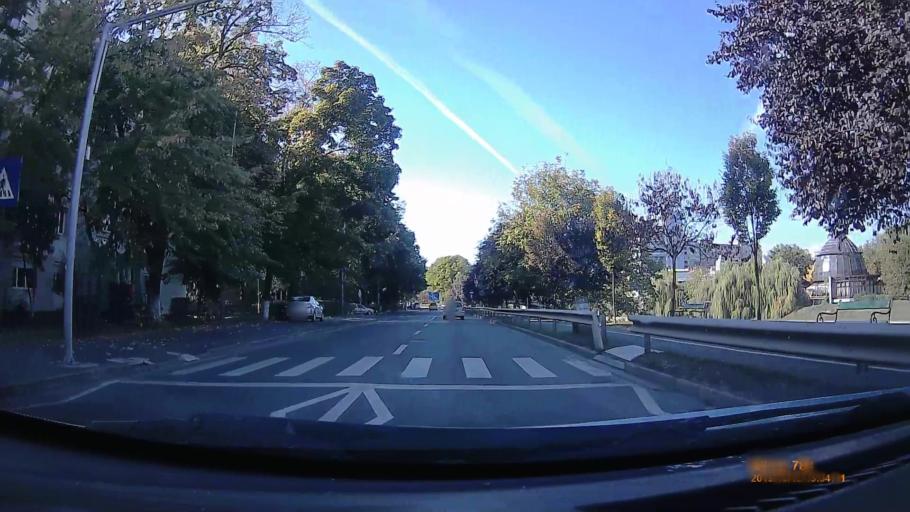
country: RO
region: Bihor
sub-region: Comuna Biharea
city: Oradea
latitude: 47.0543
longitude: 21.9446
